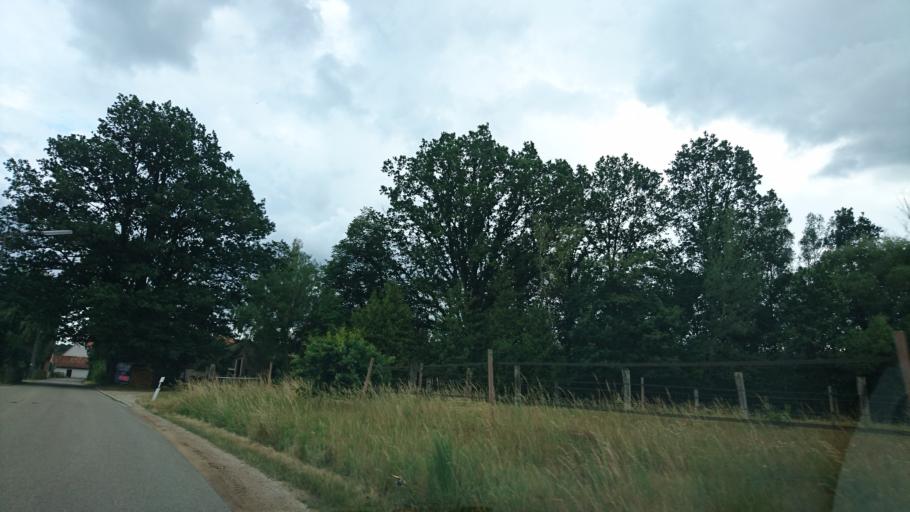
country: DE
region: Bavaria
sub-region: Regierungsbezirk Mittelfranken
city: Roth
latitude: 49.1916
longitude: 11.1061
